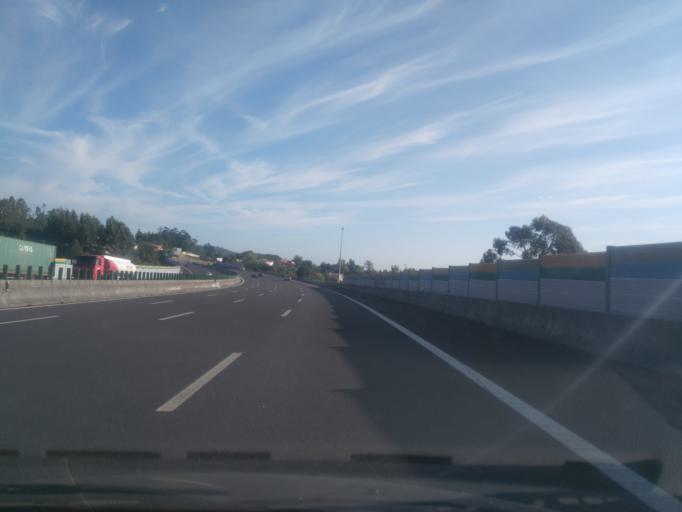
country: PT
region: Porto
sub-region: Vila Nova de Gaia
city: Grijo
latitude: 41.0354
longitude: -8.5720
